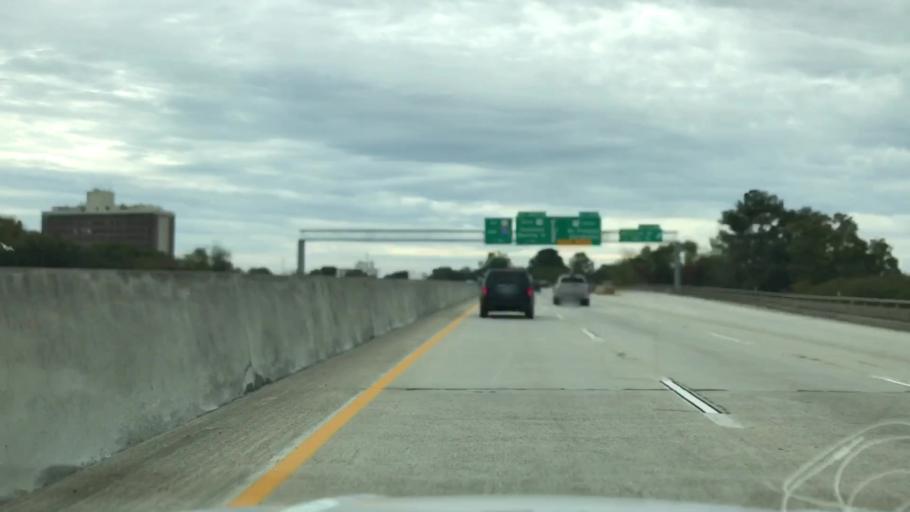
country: US
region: South Carolina
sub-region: Charleston County
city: North Charleston
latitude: 32.8155
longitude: -79.9543
